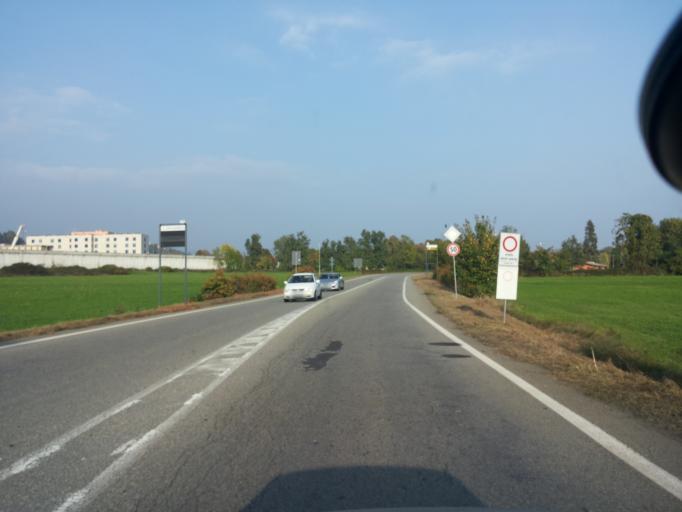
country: IT
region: Piedmont
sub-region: Provincia di Biella
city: Occhieppo Inferiore
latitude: 45.5498
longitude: 8.0335
